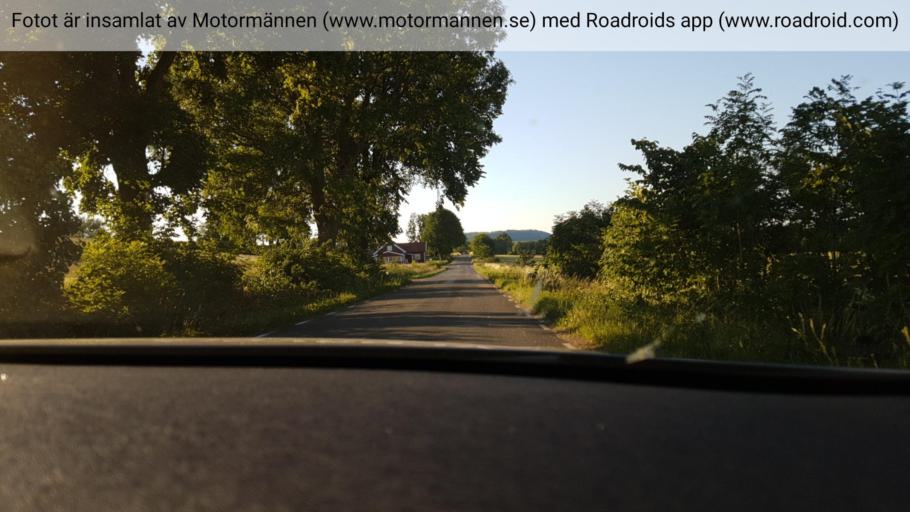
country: SE
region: Vaestra Goetaland
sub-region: Skovde Kommun
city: Skultorp
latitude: 58.2643
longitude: 13.7896
